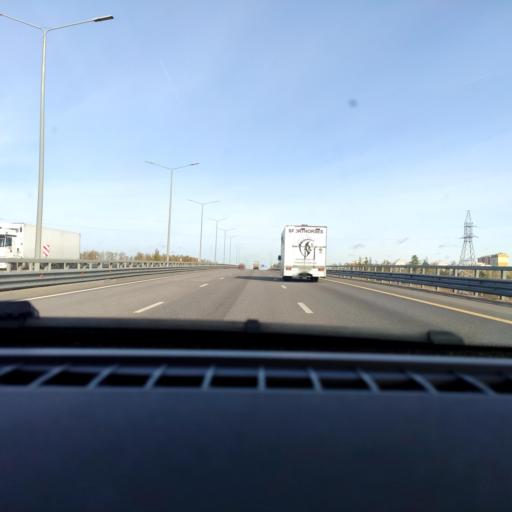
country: RU
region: Voronezj
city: Somovo
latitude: 51.7318
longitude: 39.3118
